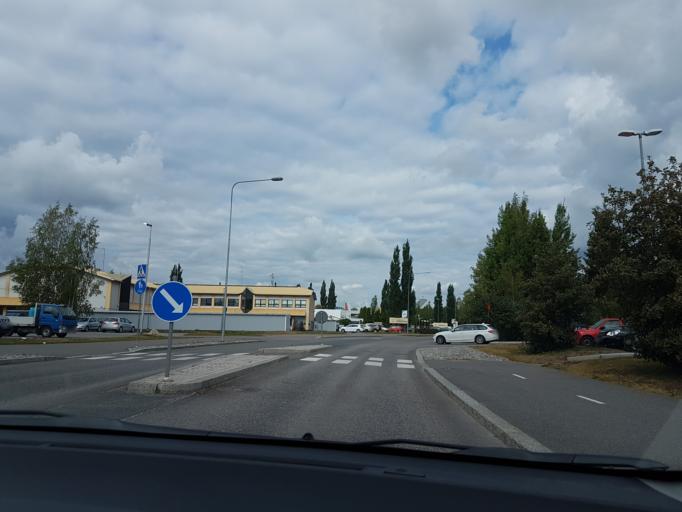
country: FI
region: Uusimaa
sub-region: Helsinki
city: Jaervenpaeae
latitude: 60.4750
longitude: 25.1107
